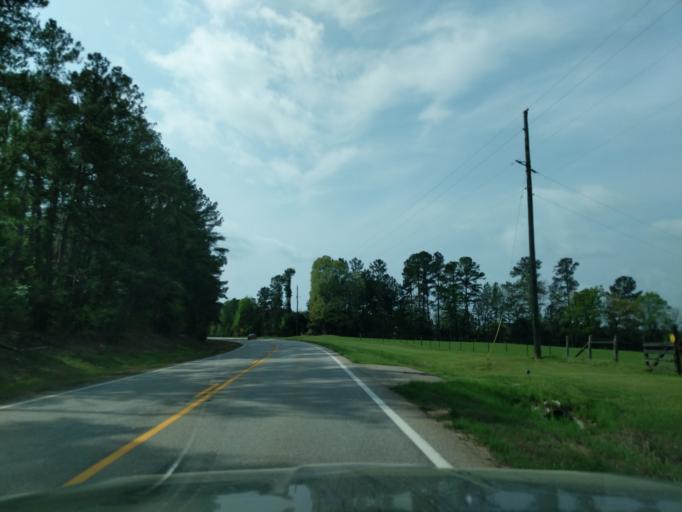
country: US
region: Georgia
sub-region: Lincoln County
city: Lincolnton
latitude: 33.7828
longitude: -82.3816
